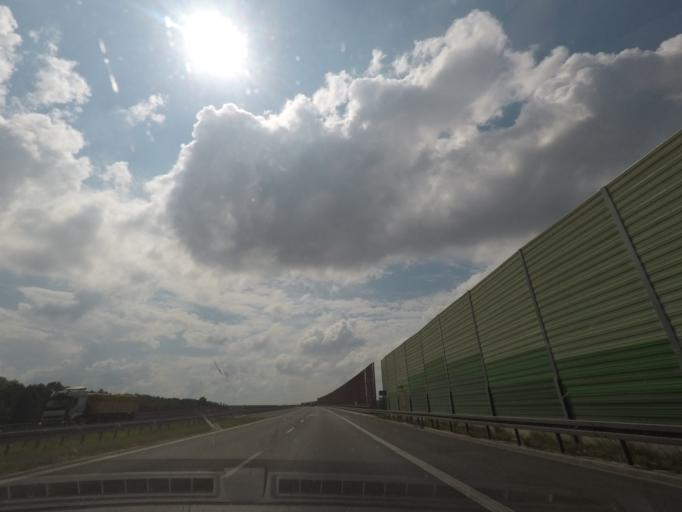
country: PL
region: Lodz Voivodeship
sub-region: Powiat kutnowski
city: Krzyzanow
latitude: 52.1423
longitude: 19.4826
